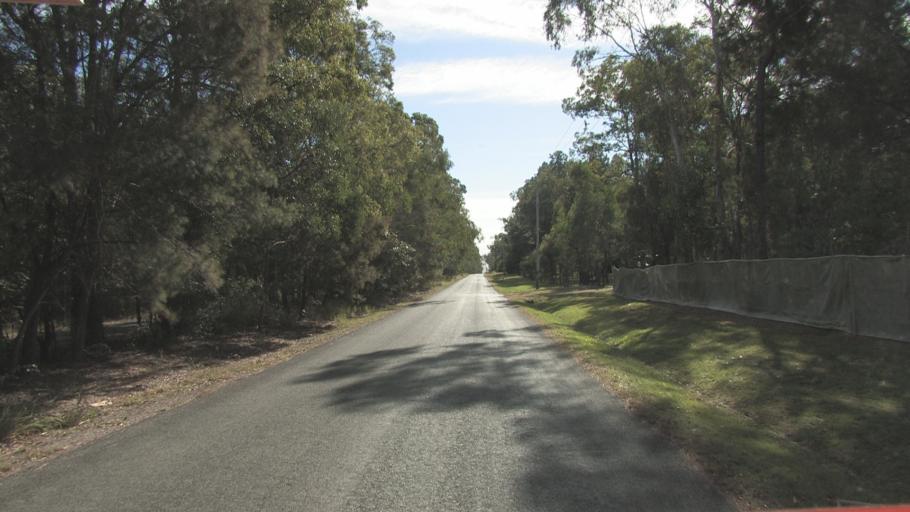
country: AU
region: Queensland
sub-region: Brisbane
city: Forest Lake
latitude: -27.6557
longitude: 152.9828
